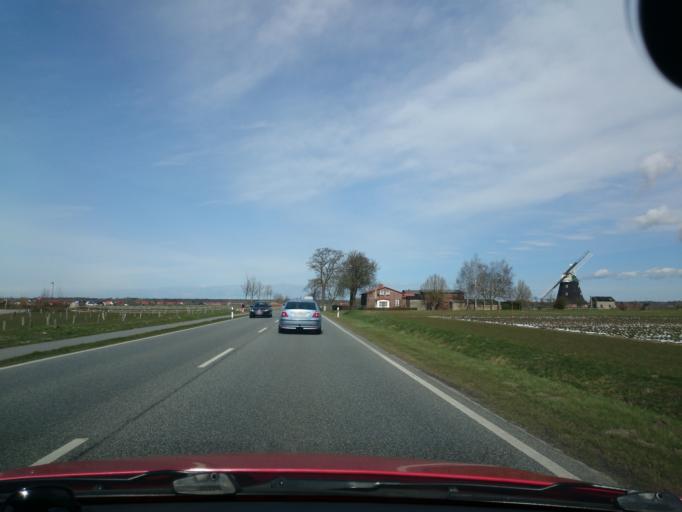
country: DE
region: Mecklenburg-Vorpommern
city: Rovershagen
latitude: 54.1620
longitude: 12.2351
